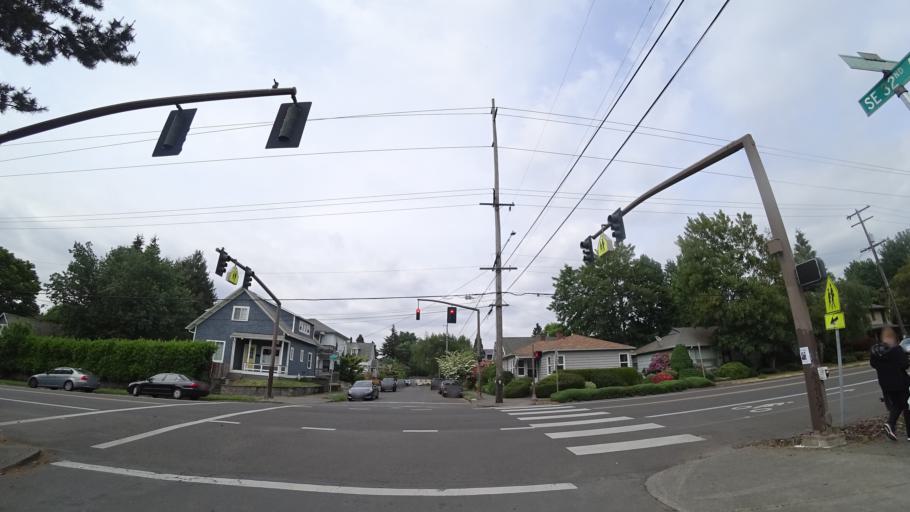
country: US
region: Oregon
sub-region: Clackamas County
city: Milwaukie
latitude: 45.4932
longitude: -122.6327
